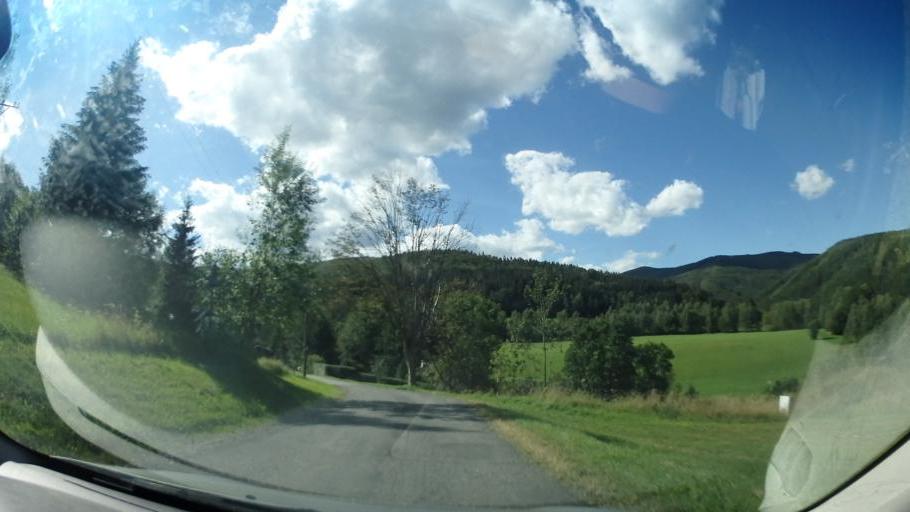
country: CZ
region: Olomoucky
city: Vapenna
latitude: 50.2251
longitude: 17.0823
